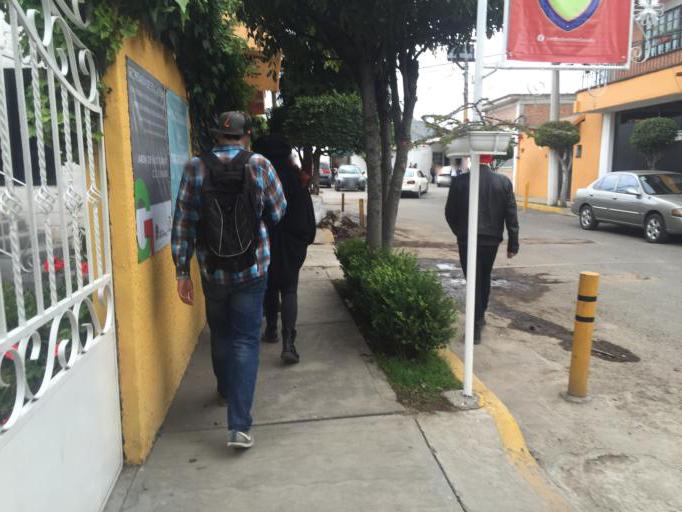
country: MX
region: Mexico
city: Ecatepec
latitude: 19.6010
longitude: -99.0441
